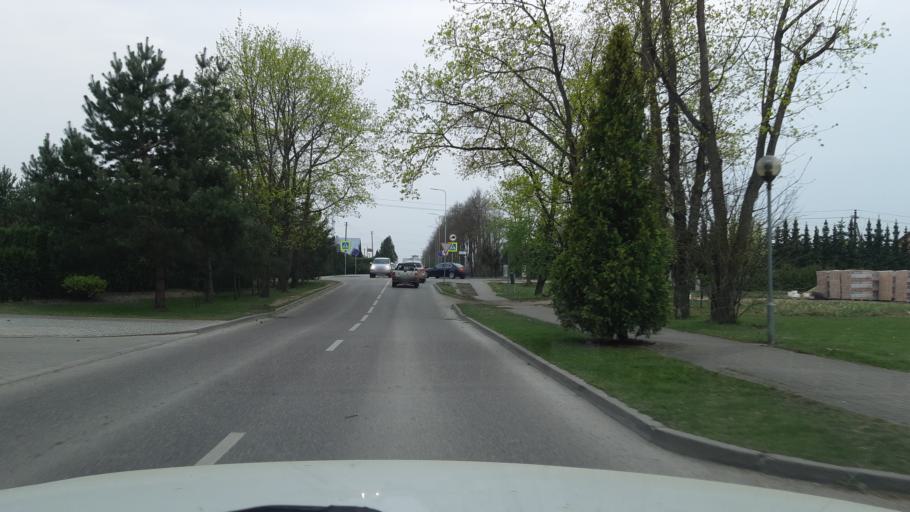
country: LT
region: Kauno apskritis
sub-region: Kaunas
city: Sargenai
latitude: 54.9425
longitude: 23.9023
